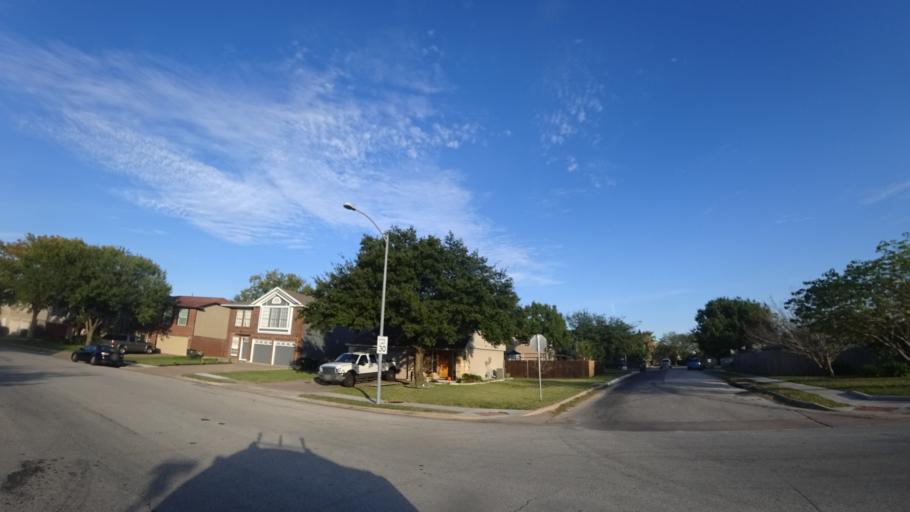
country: US
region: Texas
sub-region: Travis County
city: Pflugerville
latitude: 30.4128
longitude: -97.6499
